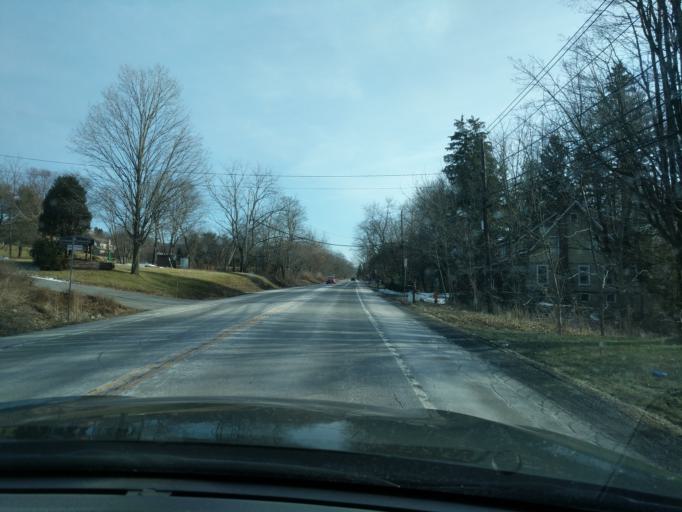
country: US
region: New York
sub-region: Tompkins County
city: East Ithaca
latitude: 42.4279
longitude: -76.4701
